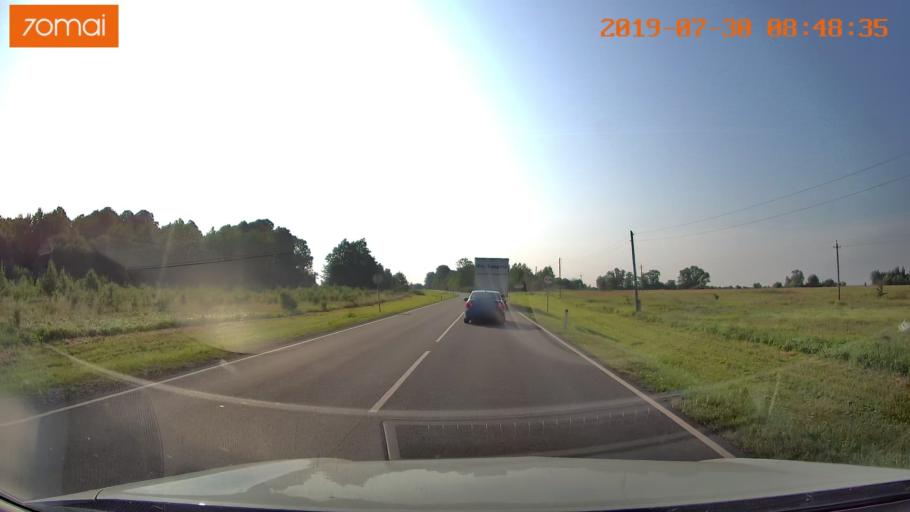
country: RU
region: Kaliningrad
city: Chernyakhovsk
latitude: 54.6169
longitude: 21.9077
